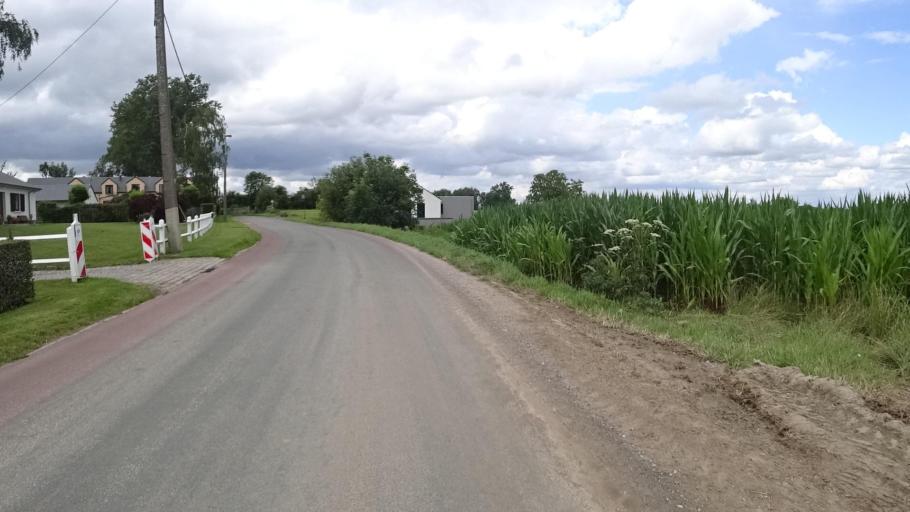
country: BE
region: Wallonia
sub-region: Province du Brabant Wallon
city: Chastre
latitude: 50.5842
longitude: 4.6010
